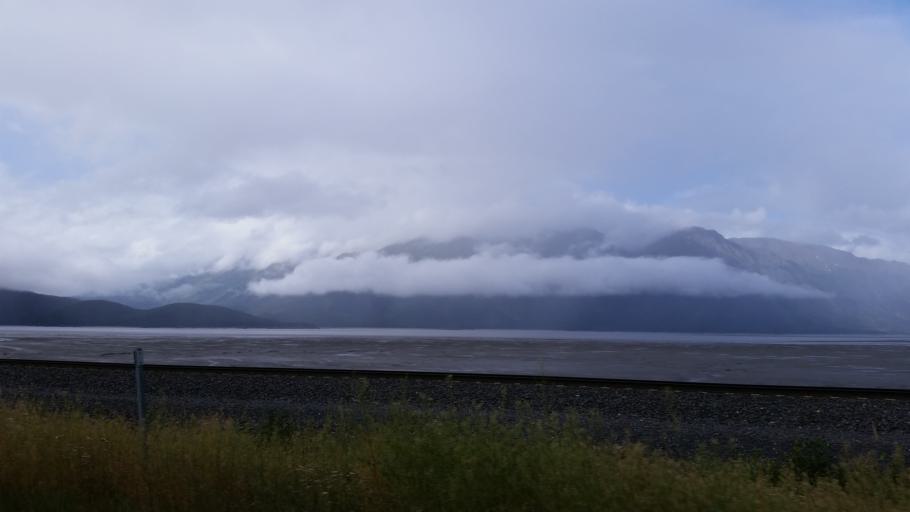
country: US
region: Alaska
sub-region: Anchorage Municipality
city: Girdwood
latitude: 60.9429
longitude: -149.3720
